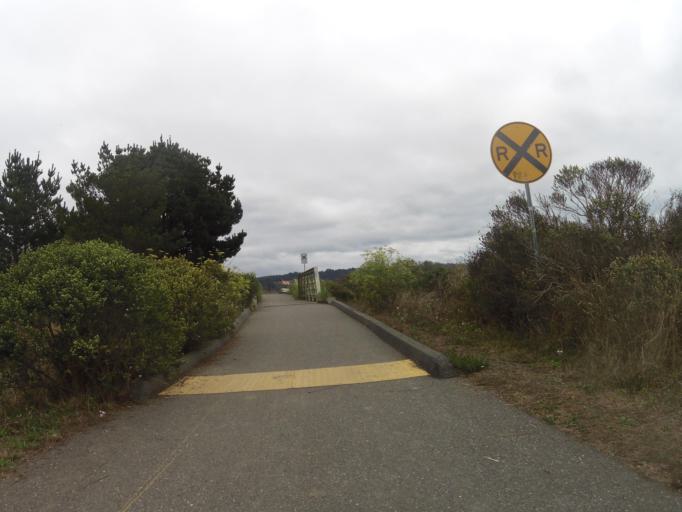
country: US
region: California
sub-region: Humboldt County
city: Bayview
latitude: 40.7595
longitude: -124.1947
